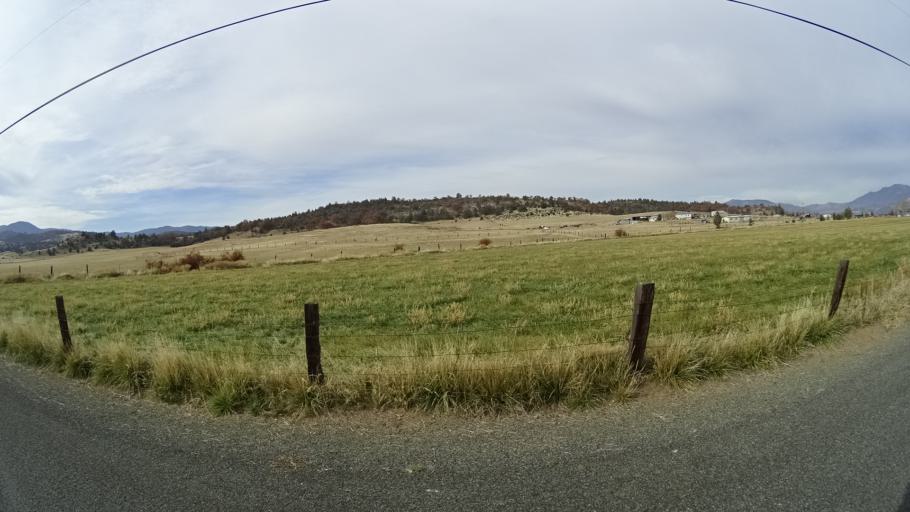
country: US
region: California
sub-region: Siskiyou County
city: Montague
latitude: 41.6996
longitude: -122.5641
